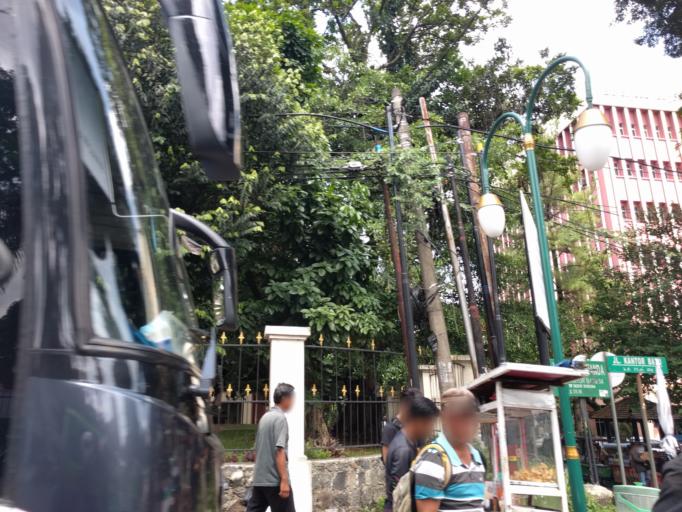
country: ID
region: West Java
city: Bogor
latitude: -6.5984
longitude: 106.7941
